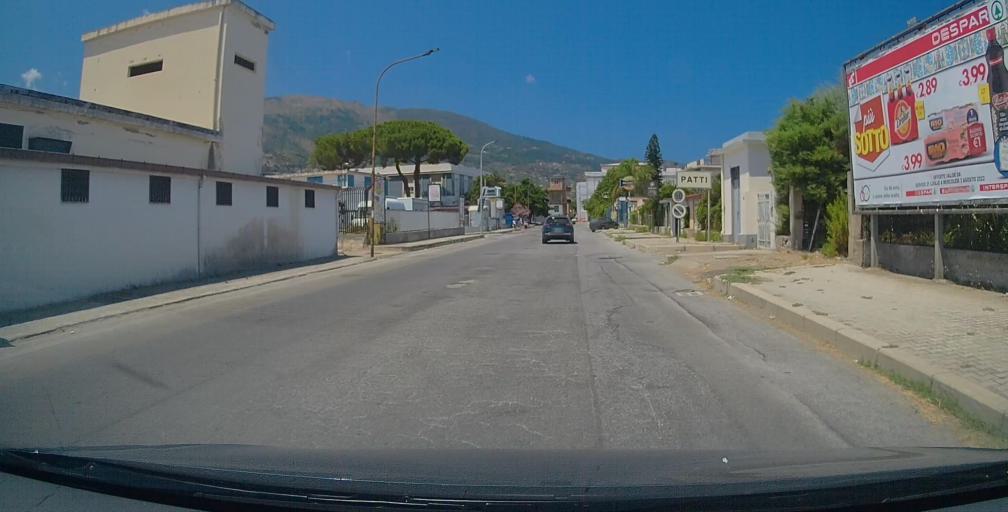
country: IT
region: Sicily
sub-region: Messina
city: Patti
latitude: 38.1493
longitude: 14.9784
